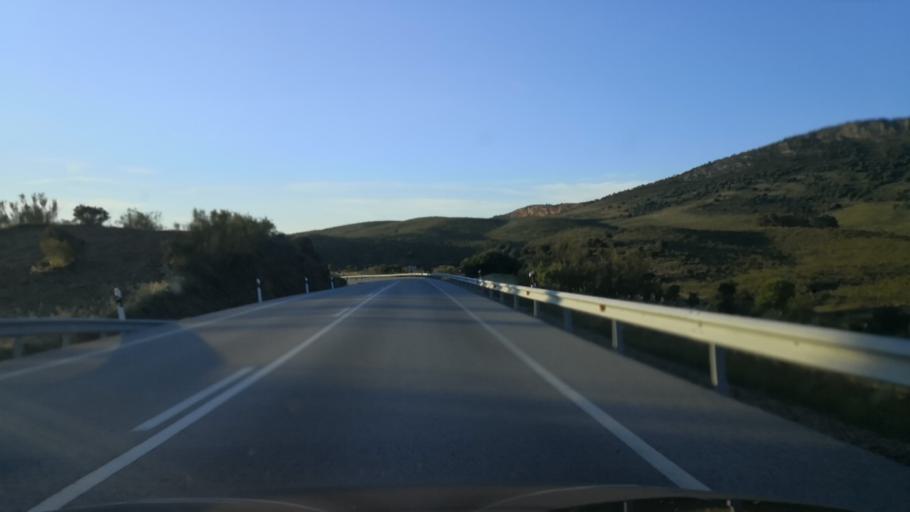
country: ES
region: Extremadura
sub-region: Provincia de Caceres
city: Valencia de Alcantara
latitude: 39.4652
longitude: -7.2039
